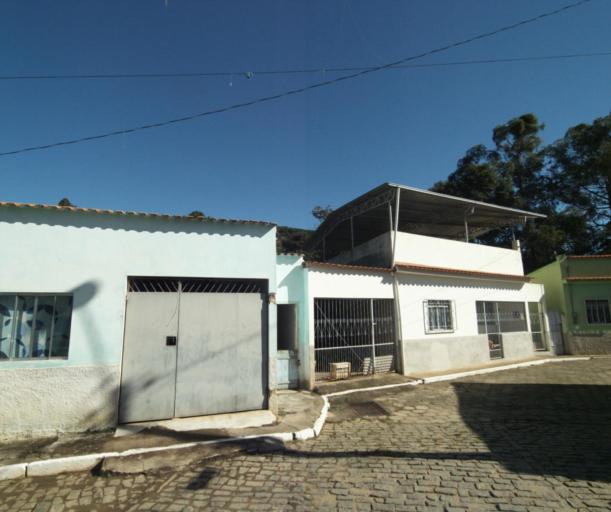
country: BR
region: Minas Gerais
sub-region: Espera Feliz
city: Espera Feliz
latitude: -20.6869
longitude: -41.8477
